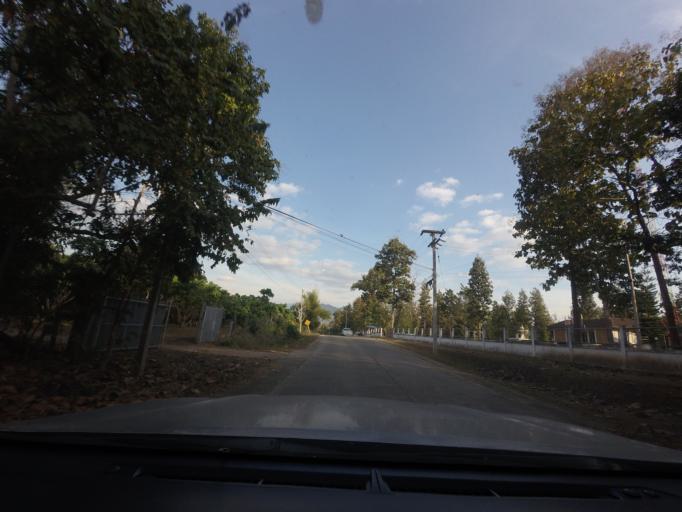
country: TH
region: Mae Hong Son
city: Wiang Nuea
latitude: 19.3862
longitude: 98.4209
